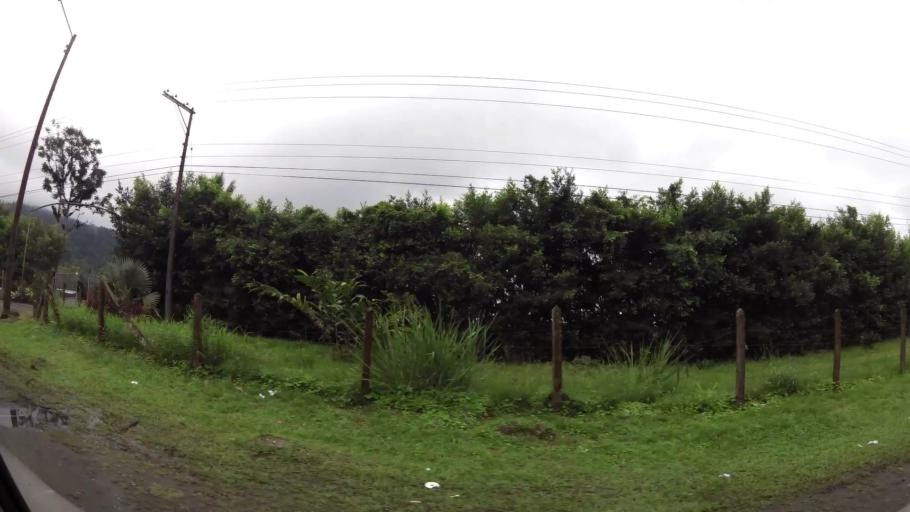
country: EC
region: Santo Domingo de los Tsachilas
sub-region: Canton Santo Domingo de los Colorados
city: Santo Domingo de los Colorados
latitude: -0.2724
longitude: -79.1070
